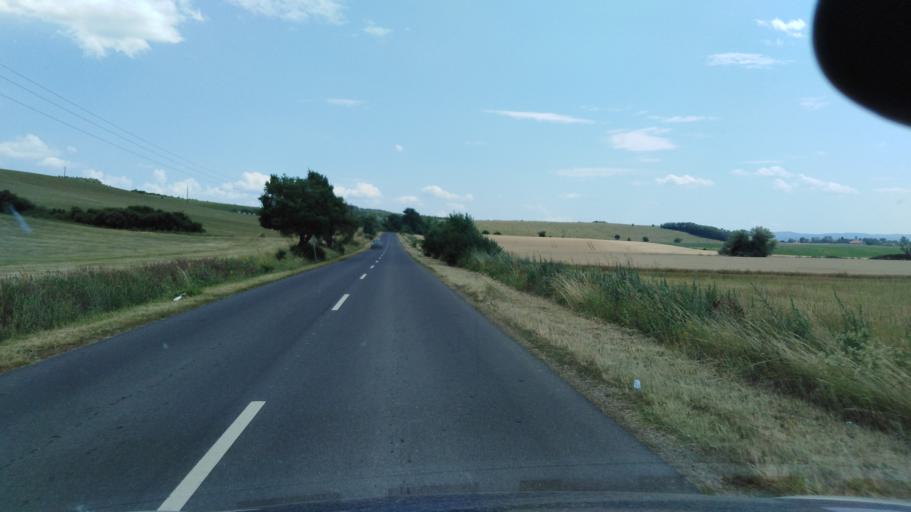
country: HU
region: Nograd
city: Szecseny
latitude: 48.1693
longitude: 19.5340
